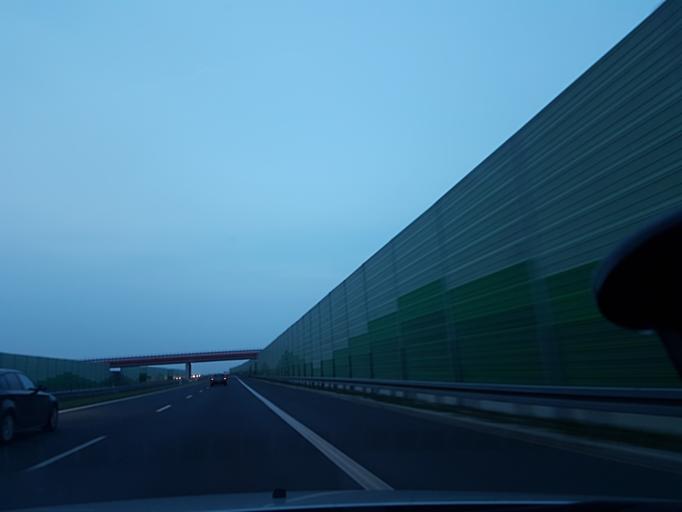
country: PL
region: Lodz Voivodeship
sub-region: Powiat leczycki
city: Piatek
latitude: 52.1036
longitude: 19.5116
